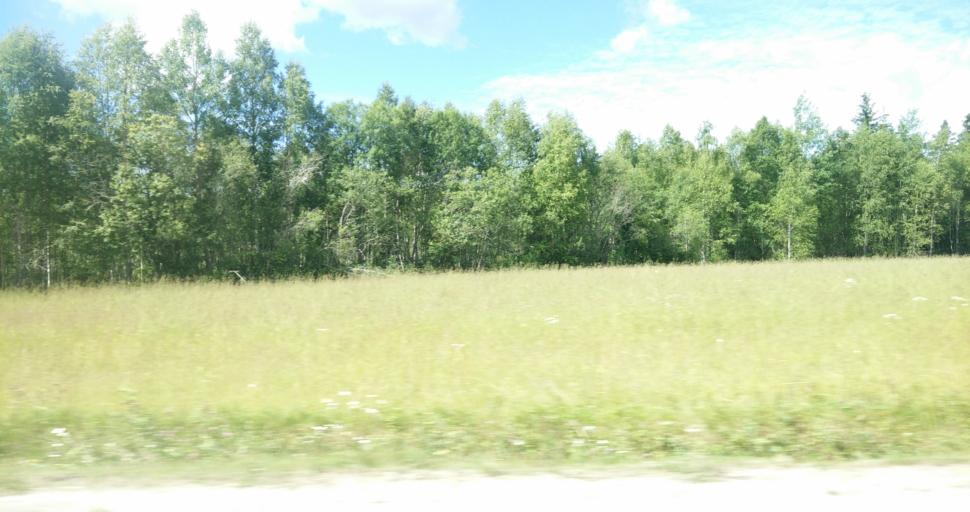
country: SE
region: Vaermland
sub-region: Hagfors Kommun
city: Ekshaerad
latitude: 60.0434
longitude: 13.4932
